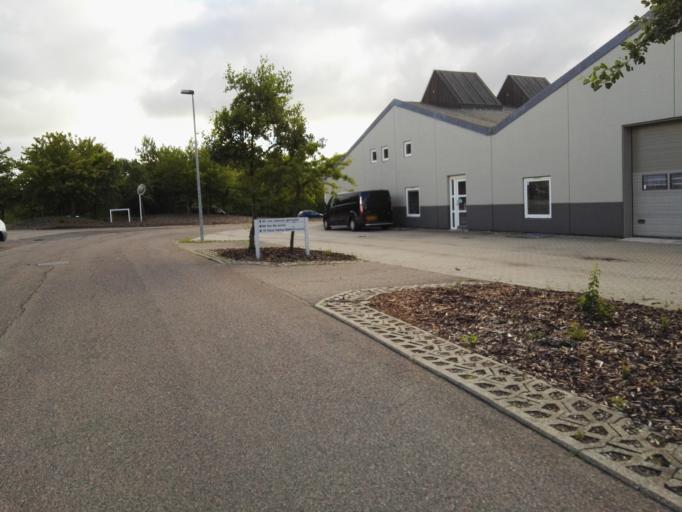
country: DK
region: Capital Region
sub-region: Egedal Kommune
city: Smorumnedre
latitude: 55.7512
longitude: 12.3042
